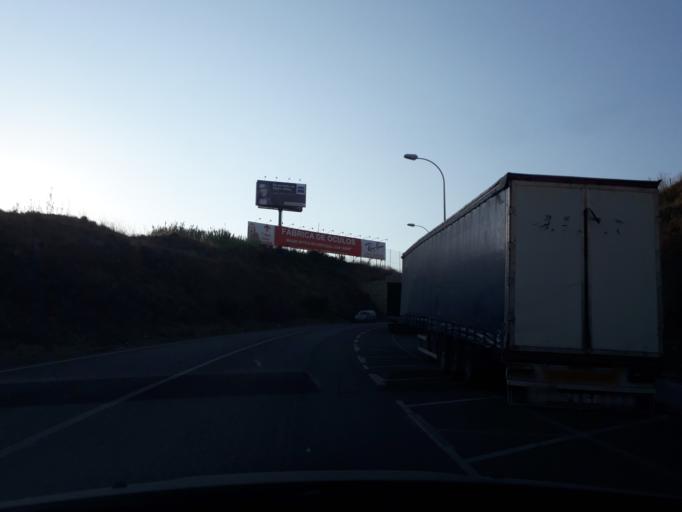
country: PT
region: Lisbon
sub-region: Amadora
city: Amadora
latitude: 38.7424
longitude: -9.2248
